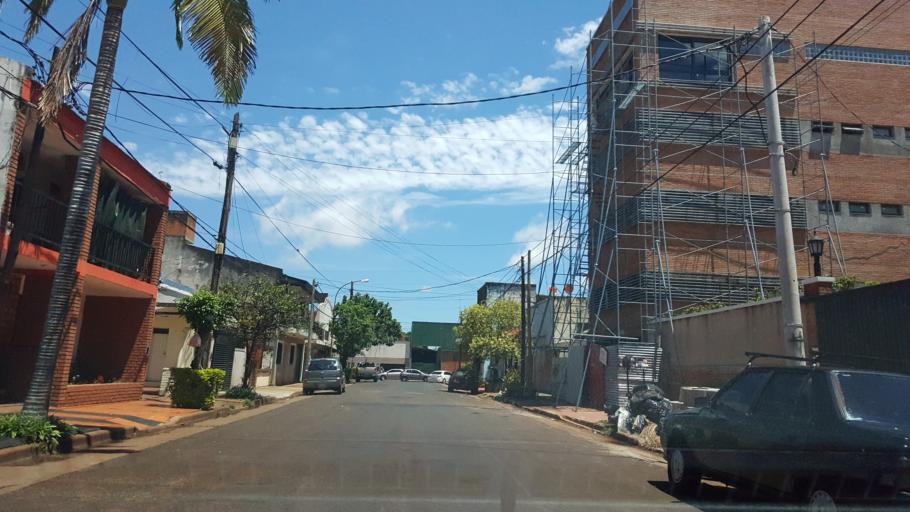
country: AR
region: Misiones
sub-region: Departamento de Capital
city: Posadas
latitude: -27.3774
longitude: -55.8941
